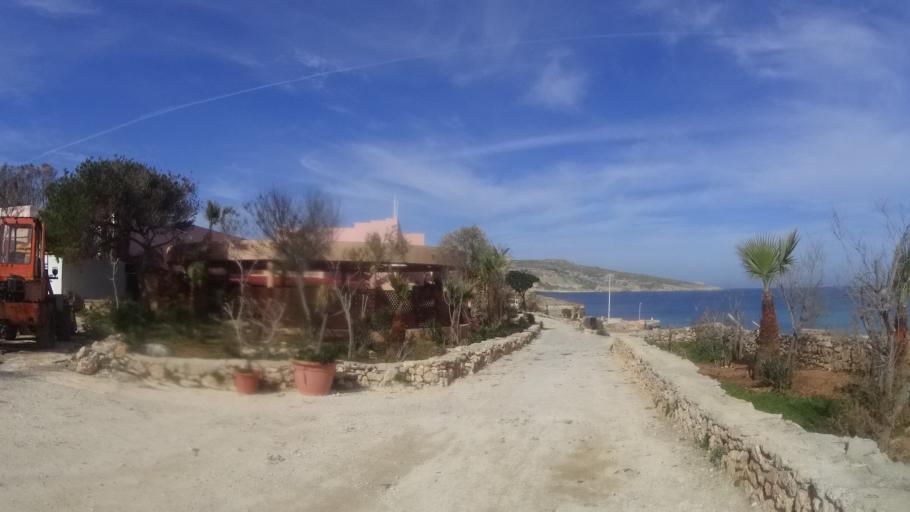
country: MT
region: Il-Qala
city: Qala
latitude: 36.0164
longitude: 14.3288
